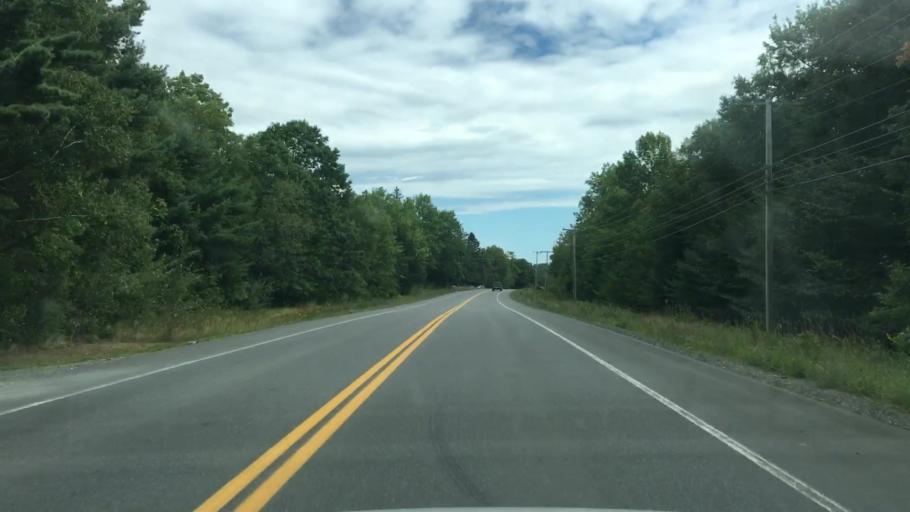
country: US
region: Maine
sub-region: Piscataquis County
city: Milo
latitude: 45.2432
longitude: -69.0168
